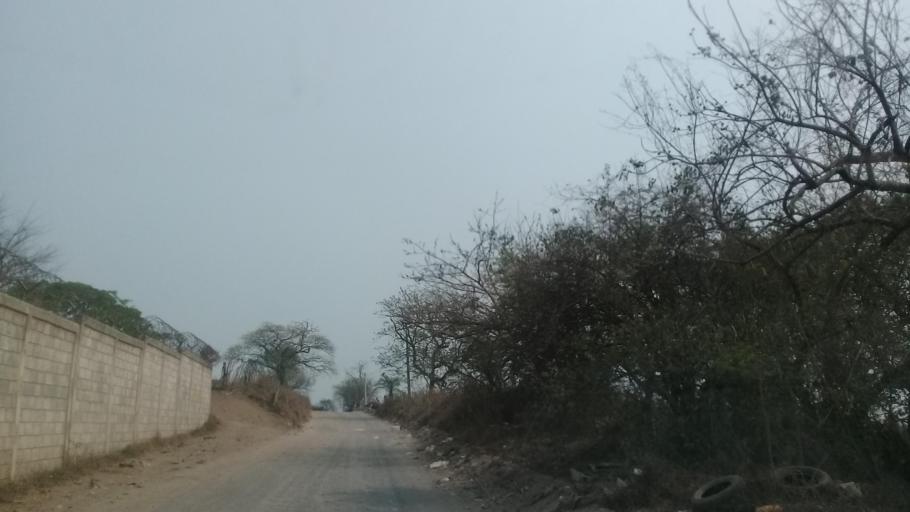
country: MX
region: Veracruz
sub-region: Veracruz
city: Oasis
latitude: 19.1906
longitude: -96.2226
